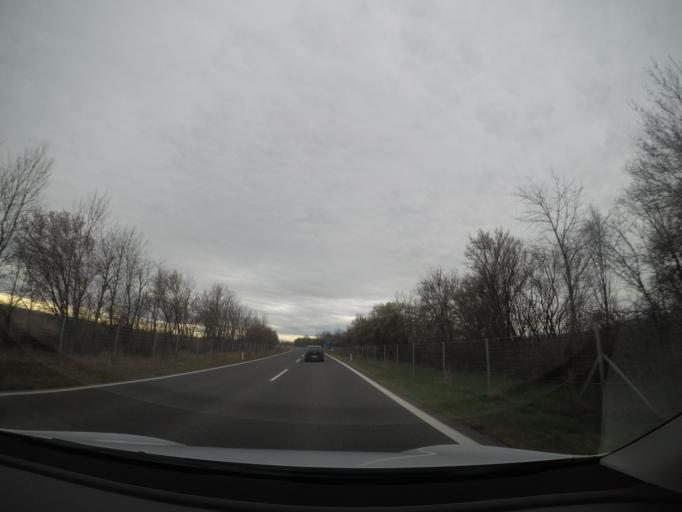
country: AT
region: Lower Austria
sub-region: Politischer Bezirk Modling
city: Munchendorf
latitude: 48.0292
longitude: 16.3598
